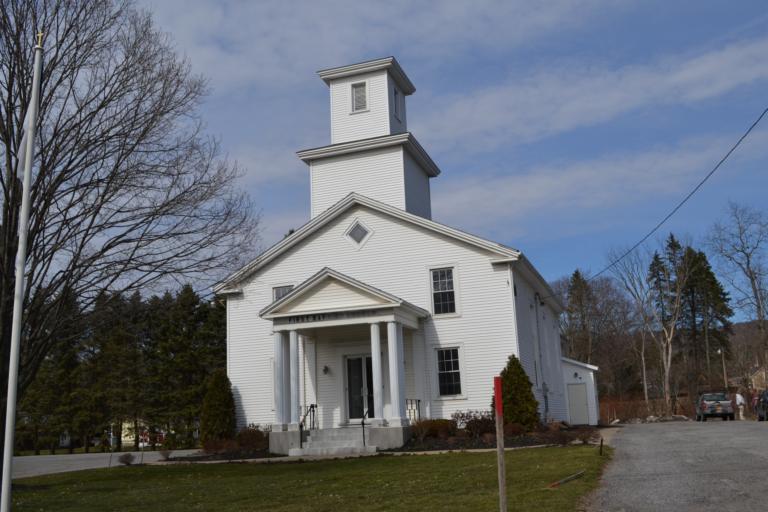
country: US
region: New York
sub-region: Erie County
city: Holland
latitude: 42.6432
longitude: -78.5453
